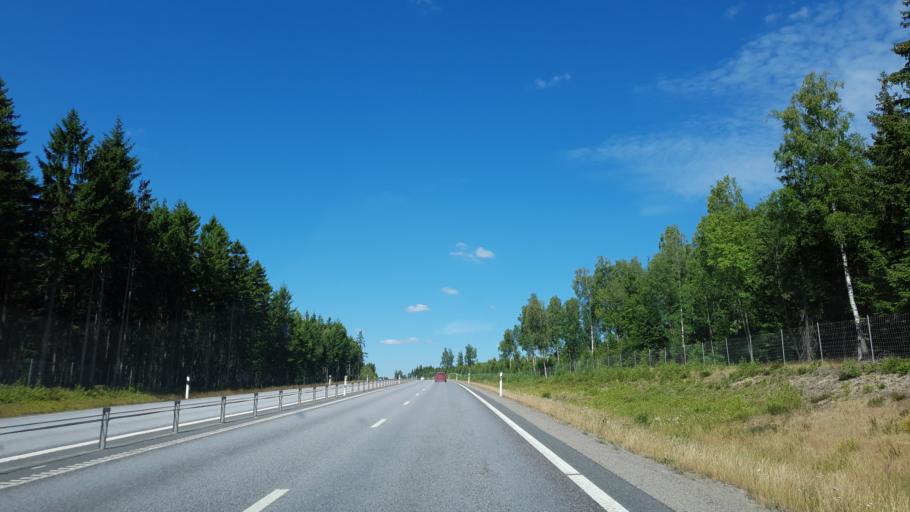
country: SE
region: Kronoberg
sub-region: Vaxjo Kommun
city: Gemla
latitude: 56.9044
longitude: 14.6625
